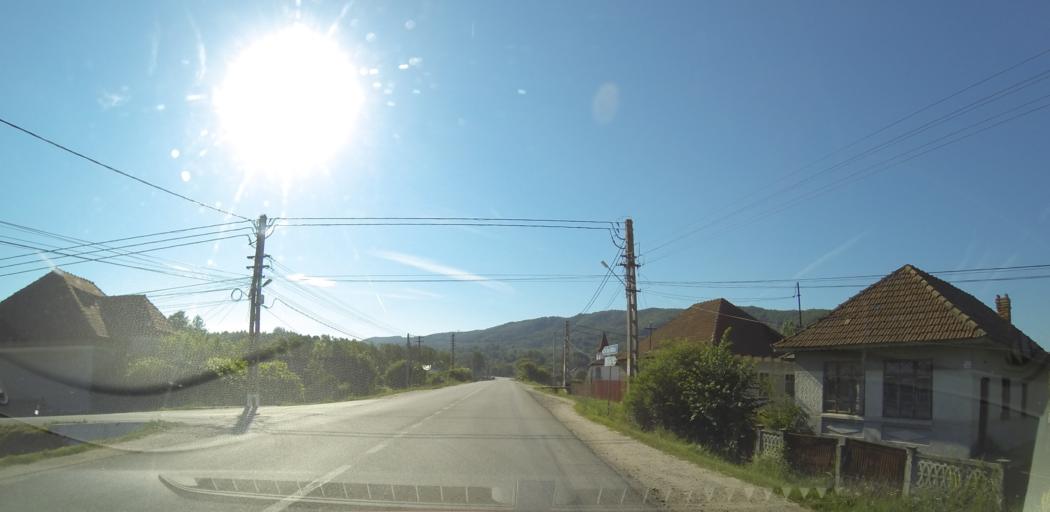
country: RO
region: Valcea
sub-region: Comuna Slatioara
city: Slatioara
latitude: 45.1204
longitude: 23.8897
